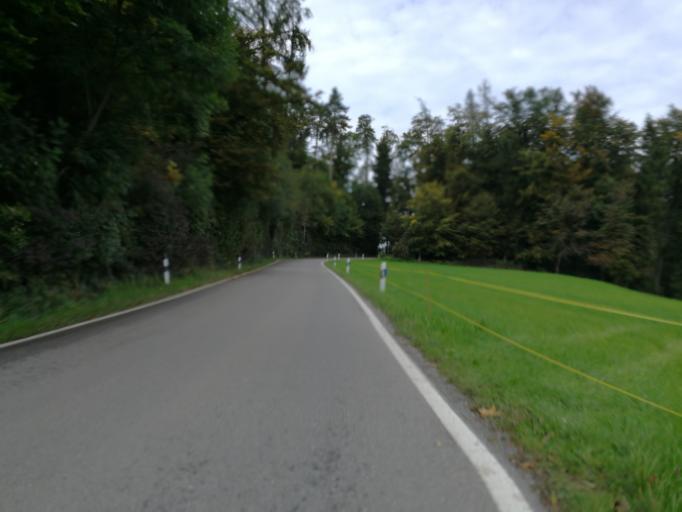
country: CH
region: Zurich
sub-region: Bezirk Meilen
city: Oetwil am See
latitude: 47.2594
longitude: 8.7200
